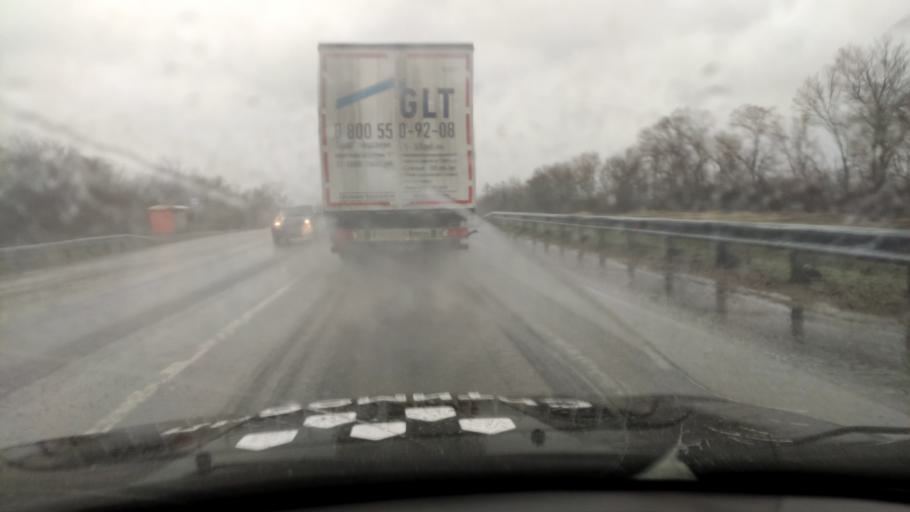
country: RU
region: Samara
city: Mezhdurechensk
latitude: 53.2578
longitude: 49.1094
